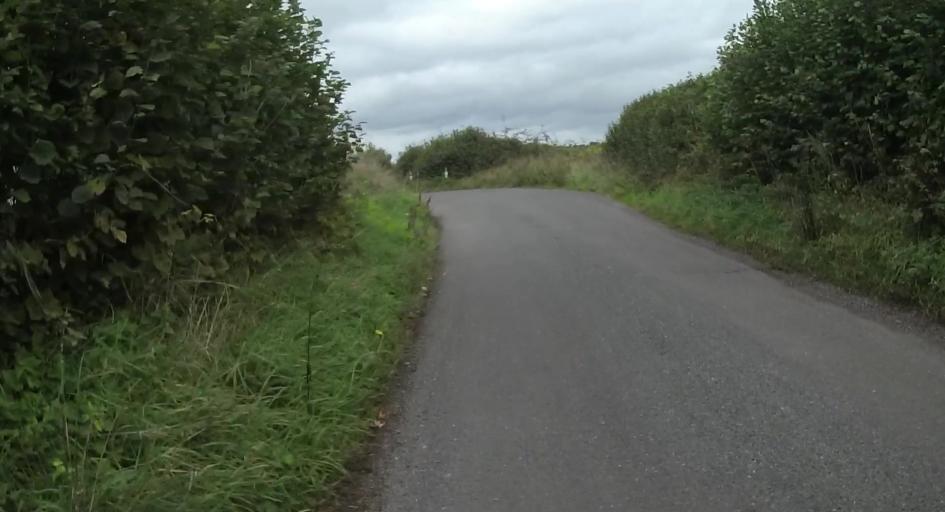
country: GB
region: England
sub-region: Hampshire
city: Alton
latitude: 51.1153
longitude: -0.9764
